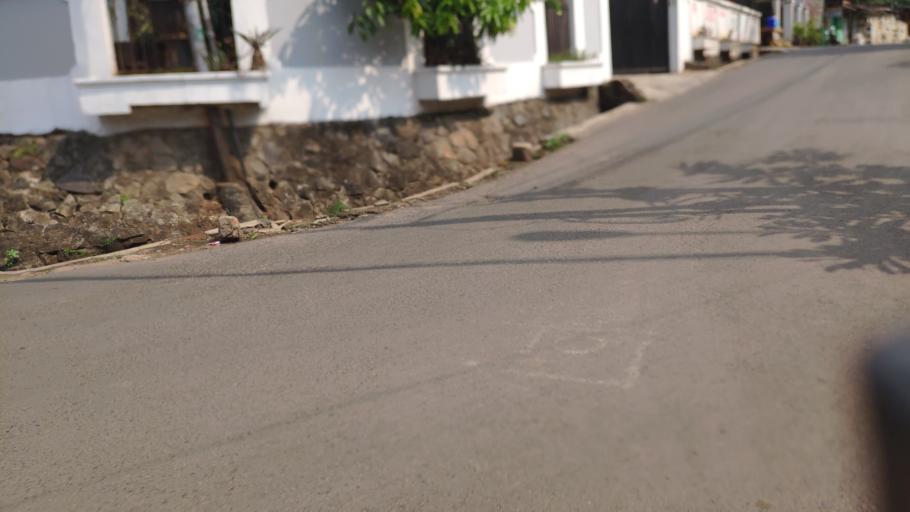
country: ID
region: Jakarta Raya
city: Jakarta
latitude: -6.3061
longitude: 106.8288
